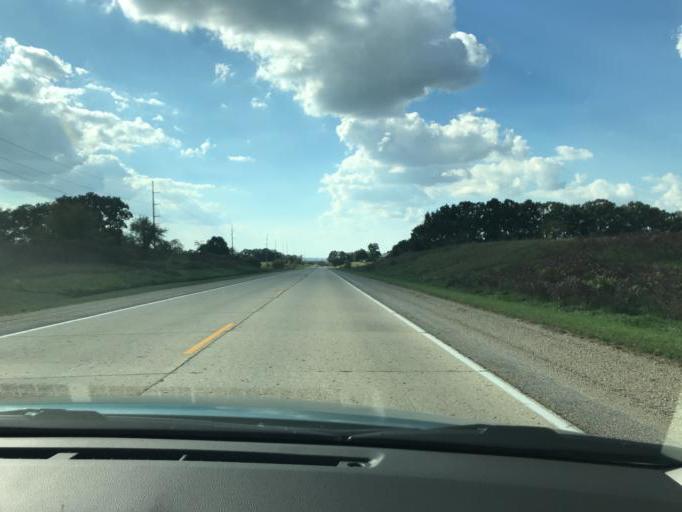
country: US
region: Wisconsin
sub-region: Rock County
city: Orfordville
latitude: 42.5587
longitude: -89.3098
